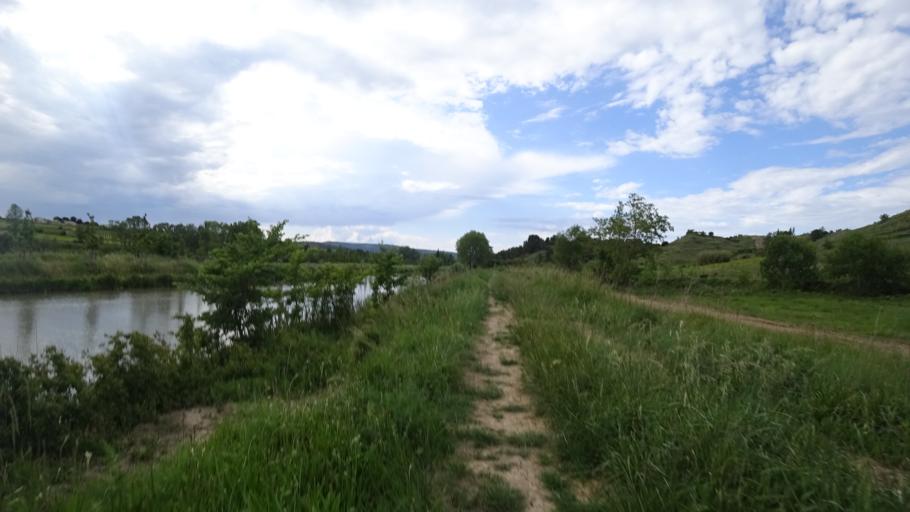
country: FR
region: Languedoc-Roussillon
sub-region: Departement de l'Aude
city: Canet
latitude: 43.2512
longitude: 2.8432
